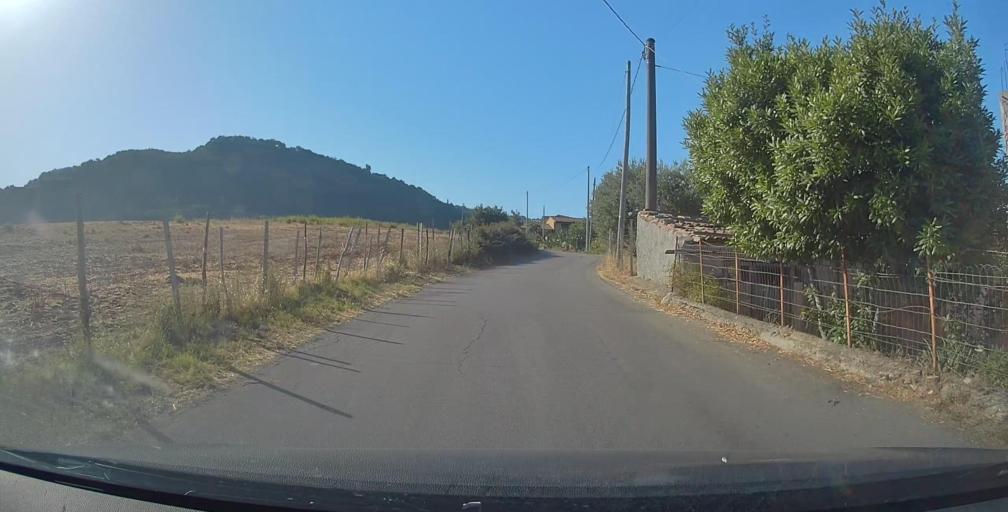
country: IT
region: Sicily
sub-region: Messina
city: San Piero Patti
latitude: 38.0691
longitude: 14.9864
